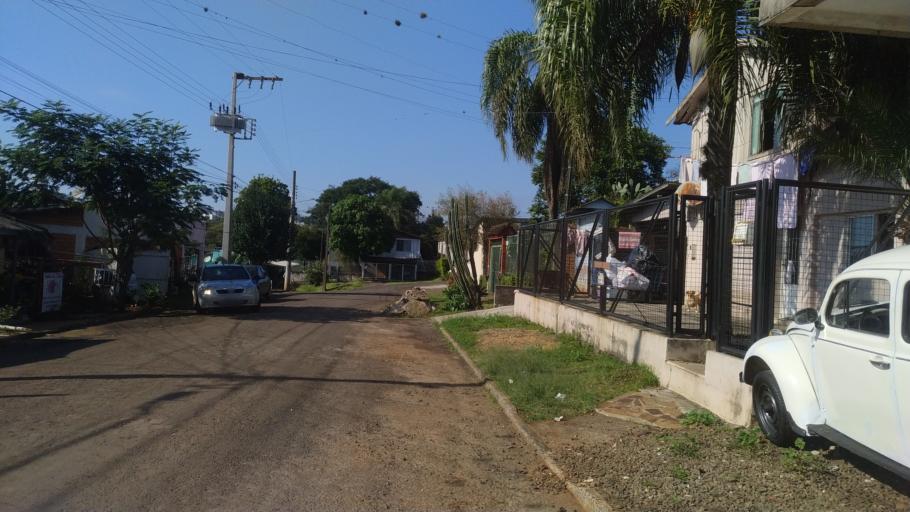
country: BR
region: Santa Catarina
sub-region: Chapeco
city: Chapeco
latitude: -27.1019
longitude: -52.6367
